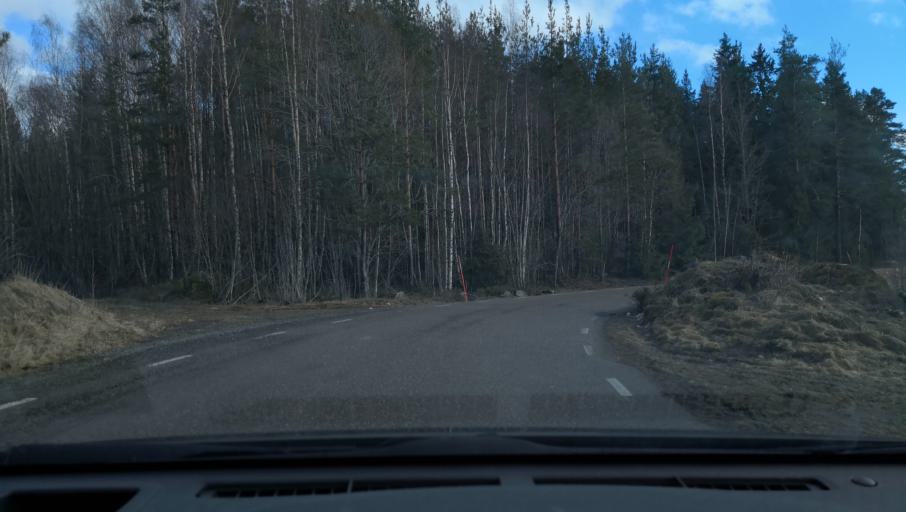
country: SE
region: Vaestmanland
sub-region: Arboga Kommun
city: Arboga
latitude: 59.3388
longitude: 15.7027
